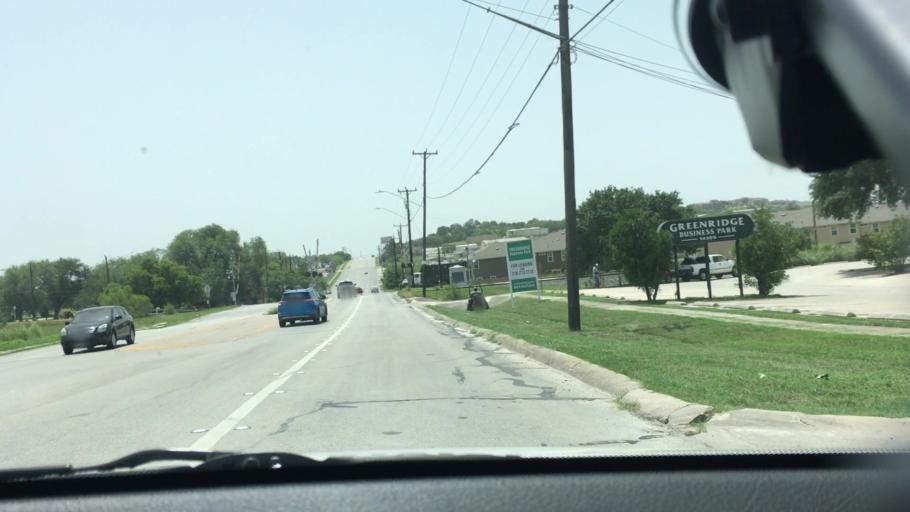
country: US
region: Texas
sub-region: Bexar County
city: Live Oak
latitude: 29.5709
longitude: -98.3572
